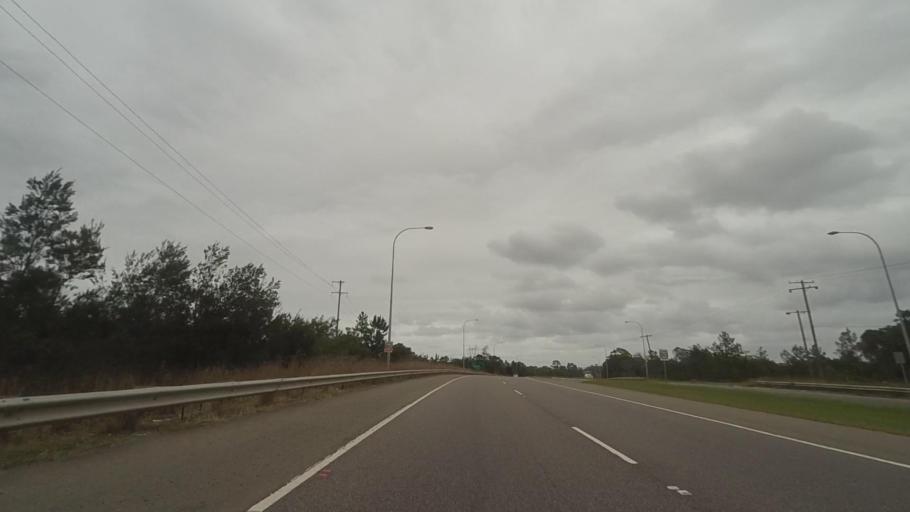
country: AU
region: New South Wales
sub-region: Wyong Shire
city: Buff Point
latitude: -33.2034
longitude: 151.5202
